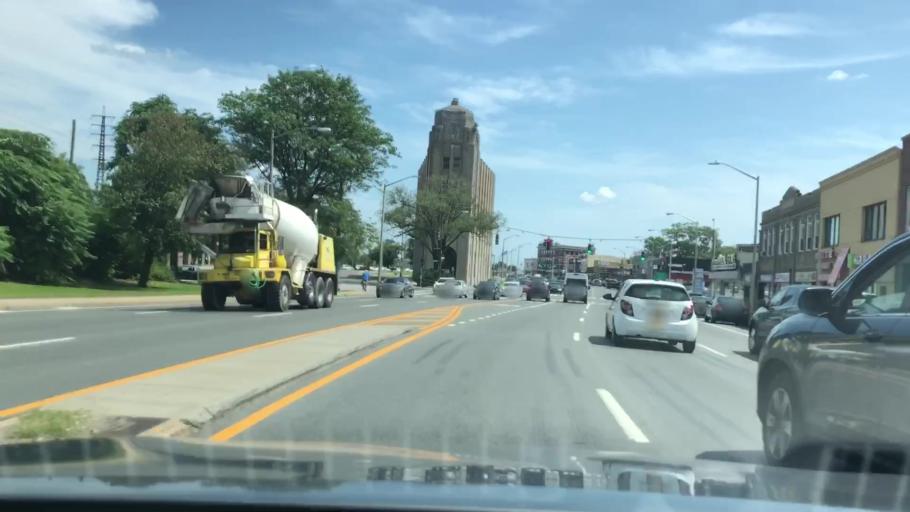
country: US
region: New York
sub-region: Nassau County
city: Freeport
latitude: 40.6567
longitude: -73.5865
